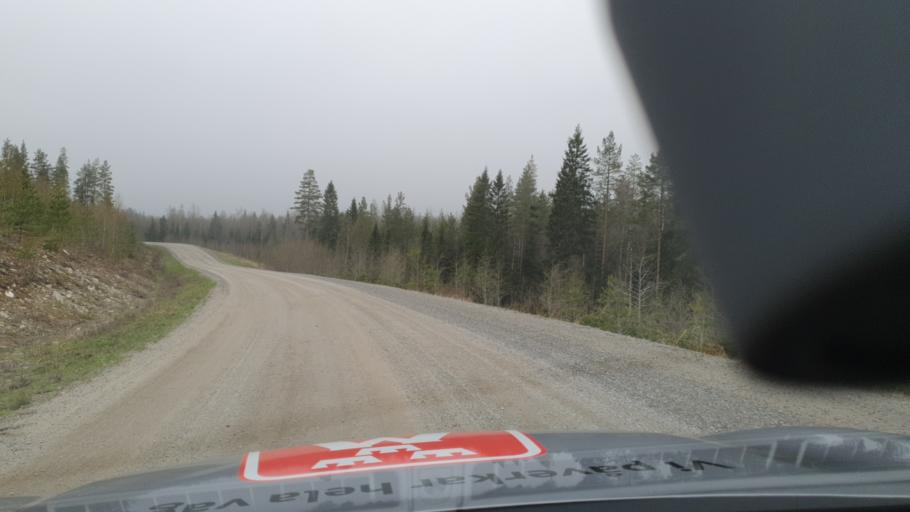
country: SE
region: Vaesternorrland
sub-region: OErnskoeldsviks Kommun
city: Husum
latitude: 63.5994
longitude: 19.0164
